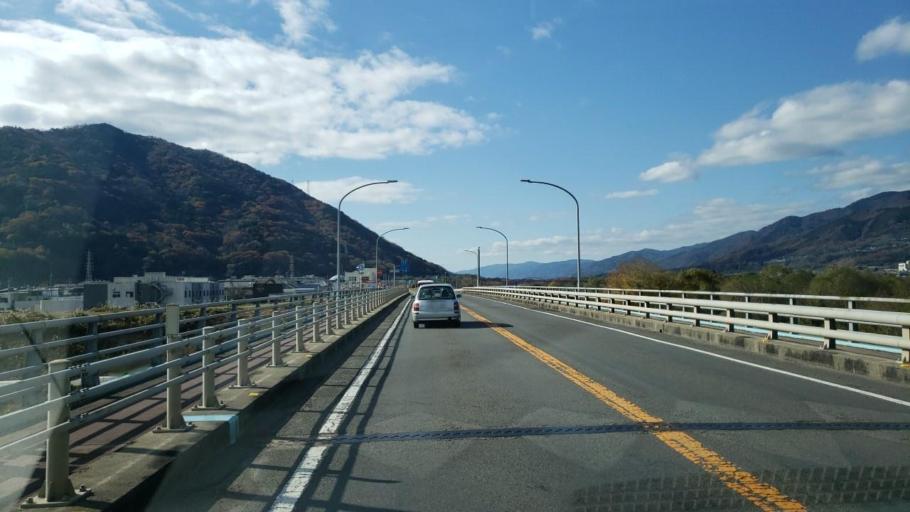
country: JP
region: Tokushima
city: Wakimachi
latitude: 34.0440
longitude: 134.0660
